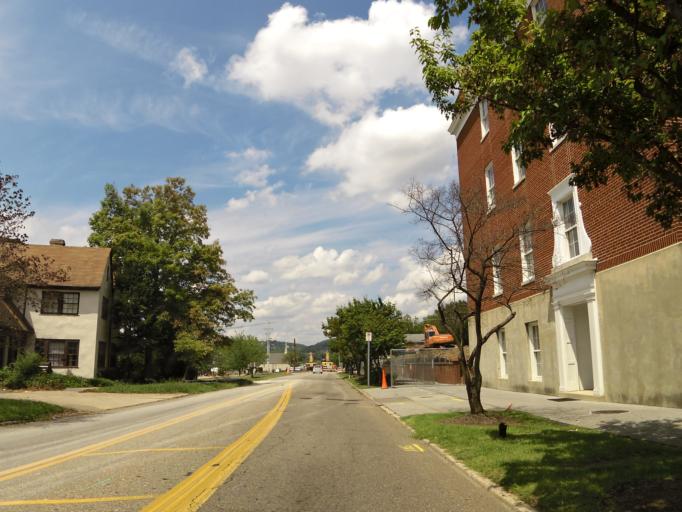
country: US
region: Tennessee
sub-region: Sullivan County
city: Kingsport
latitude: 36.5500
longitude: -82.5592
